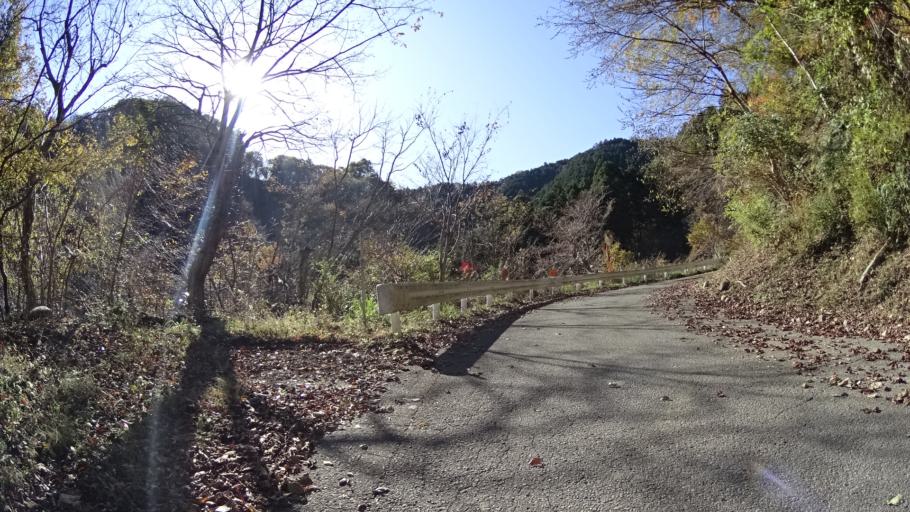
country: JP
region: Kanagawa
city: Atsugi
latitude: 35.5104
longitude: 139.2695
